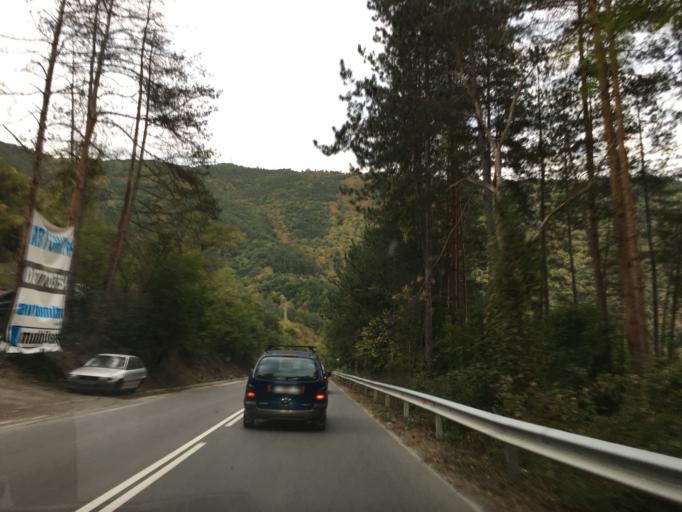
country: BG
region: Sofiya
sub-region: Obshtina Svoge
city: Svoge
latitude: 42.9456
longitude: 23.3803
